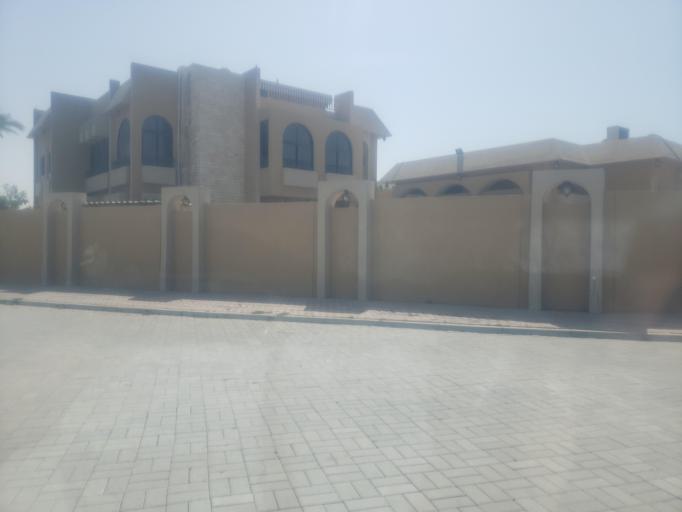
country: AE
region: Ra's al Khaymah
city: Ras al-Khaimah
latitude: 25.8155
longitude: 55.9666
